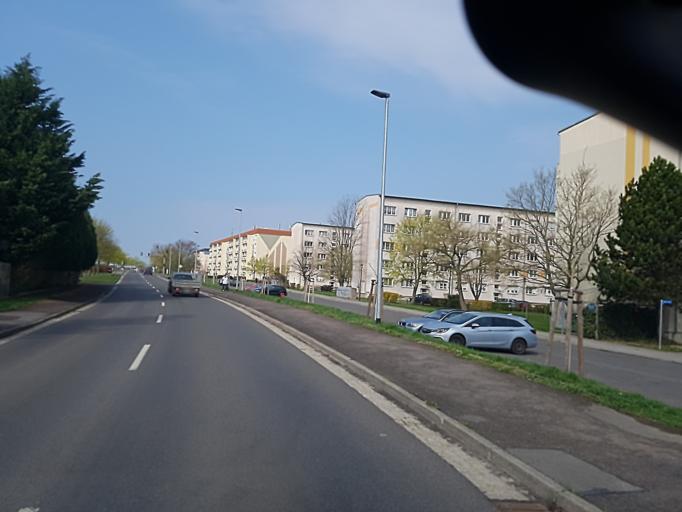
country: DE
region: Saxony
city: Zinna
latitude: 51.5654
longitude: 12.9701
